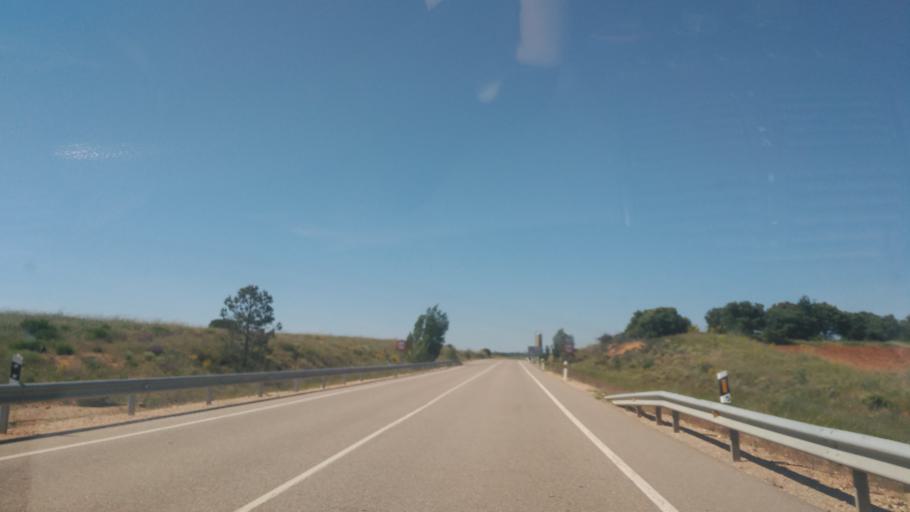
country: ES
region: Castille and Leon
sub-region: Provincia de Zamora
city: Cuelgamures
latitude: 41.2420
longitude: -5.7068
